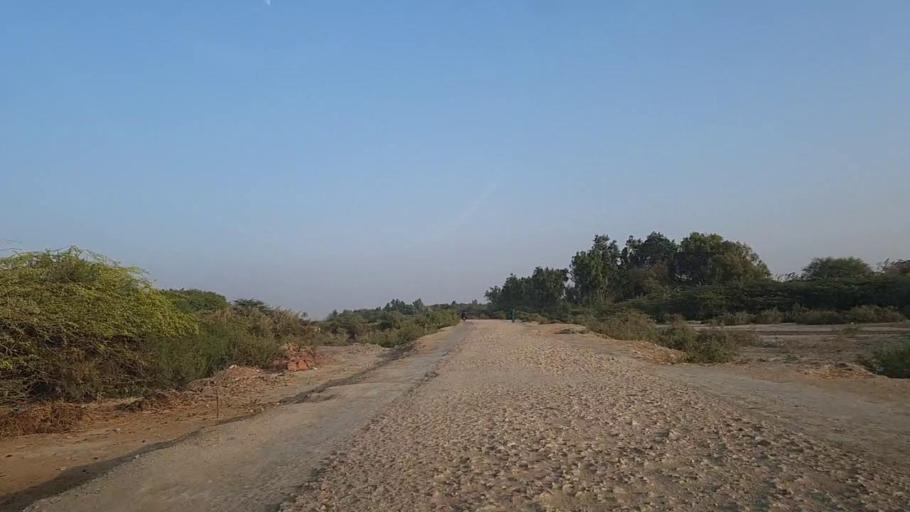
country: PK
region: Sindh
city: Keti Bandar
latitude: 24.2723
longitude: 67.6764
